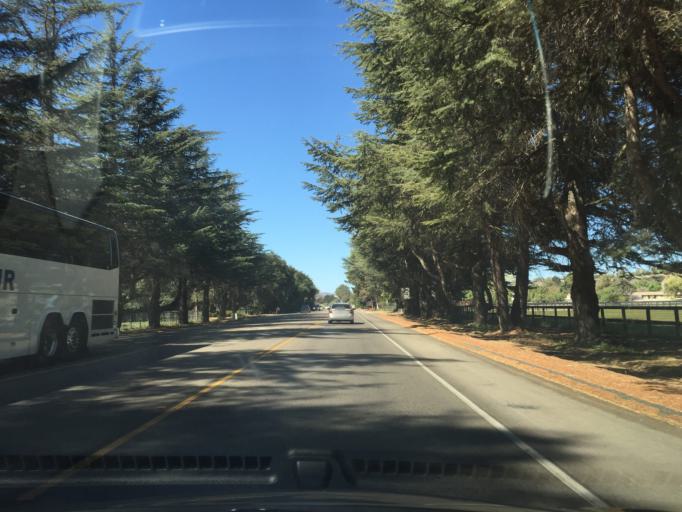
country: US
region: California
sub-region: Santa Barbara County
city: Buellton
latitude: 34.6051
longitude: -120.1729
